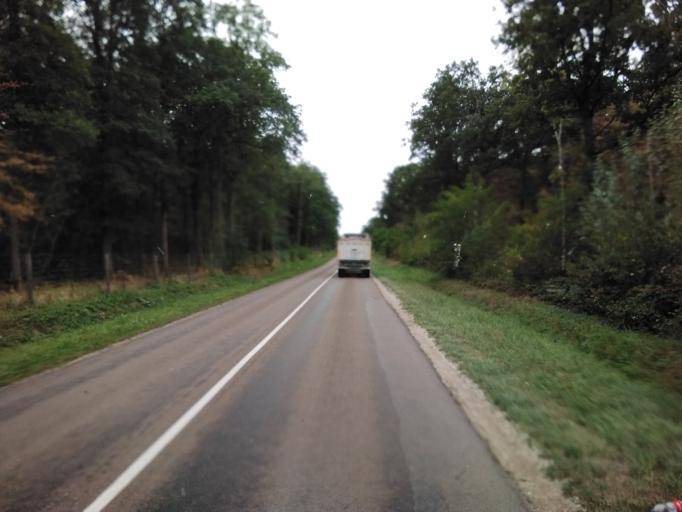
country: FR
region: Champagne-Ardenne
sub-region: Departement de l'Aube
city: Vendeuvre-sur-Barse
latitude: 48.2684
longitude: 4.5040
